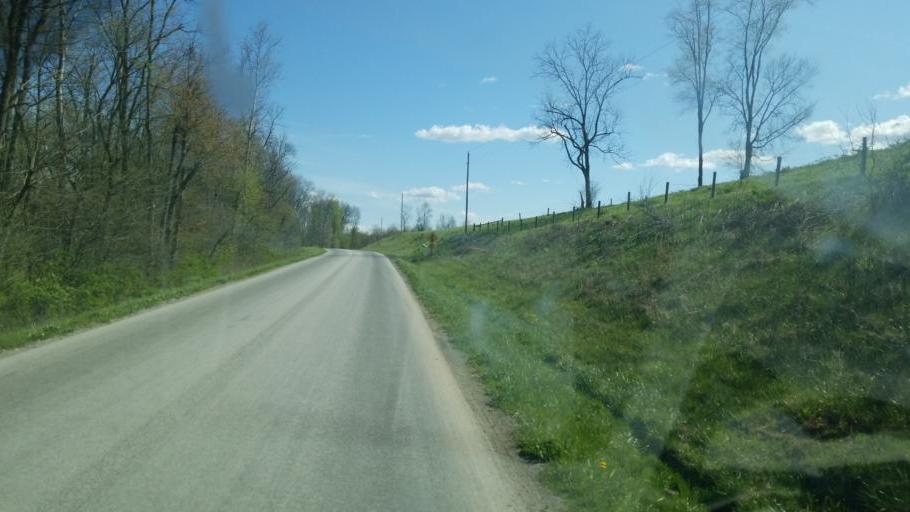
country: US
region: Ohio
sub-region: Coshocton County
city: Coshocton
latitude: 40.4158
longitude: -81.8324
